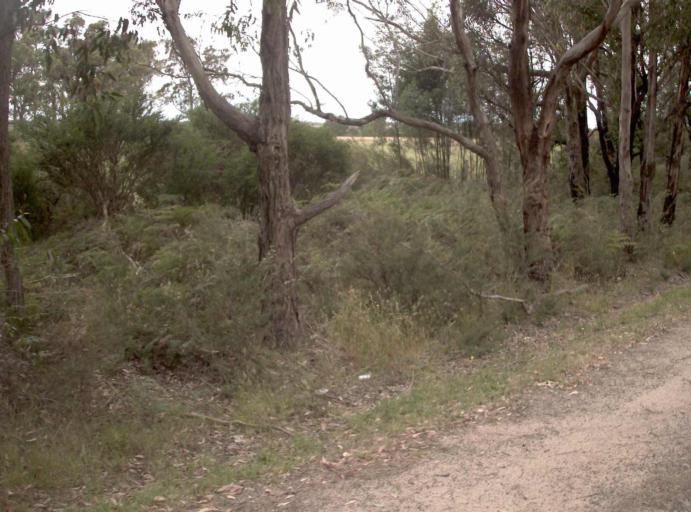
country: AU
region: Victoria
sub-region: Latrobe
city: Traralgon
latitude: -38.5086
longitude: 146.8475
